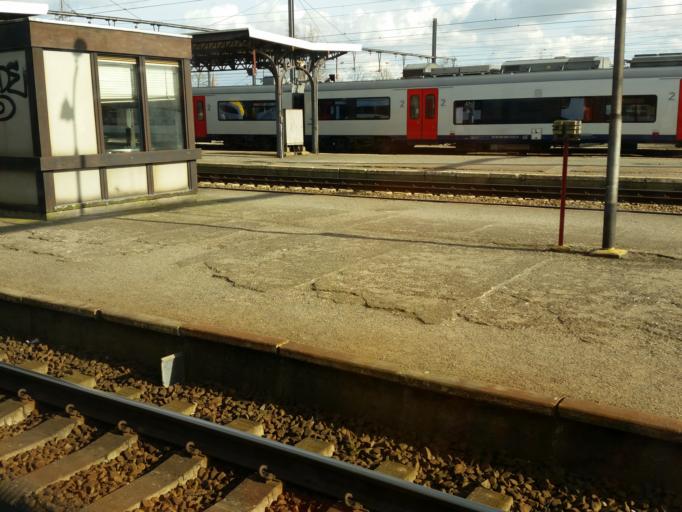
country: BE
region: Flanders
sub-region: Provincie Oost-Vlaanderen
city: Dendermonde
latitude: 51.0227
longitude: 4.1001
